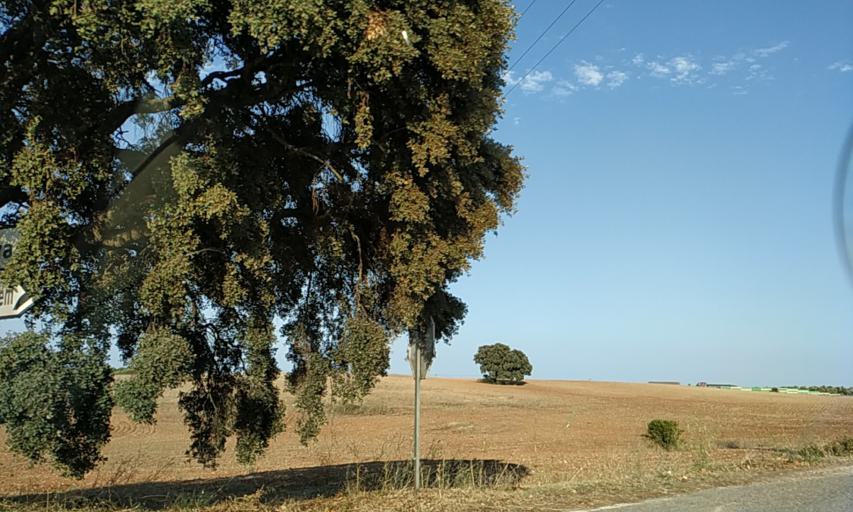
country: PT
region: Santarem
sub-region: Alcanena
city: Alcanena
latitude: 39.3992
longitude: -8.6425
